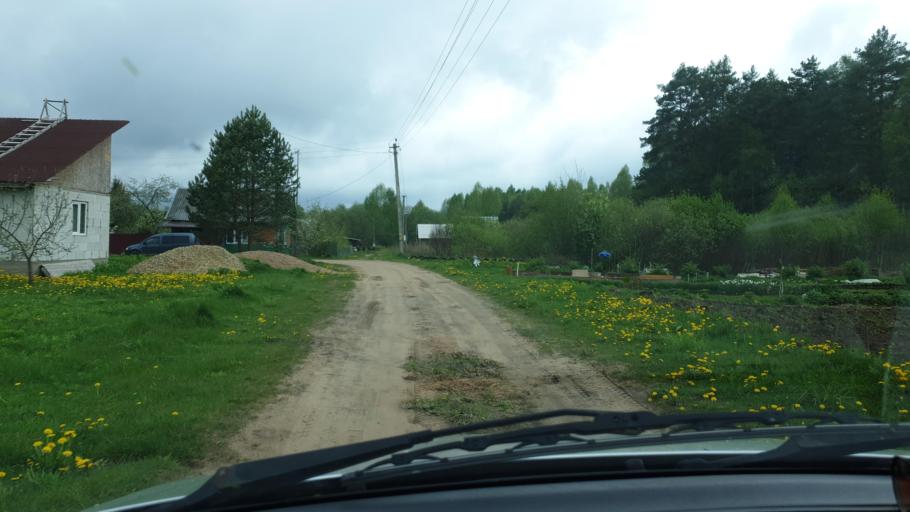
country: BY
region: Vitebsk
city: Lyepyel'
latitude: 54.9194
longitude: 28.5217
